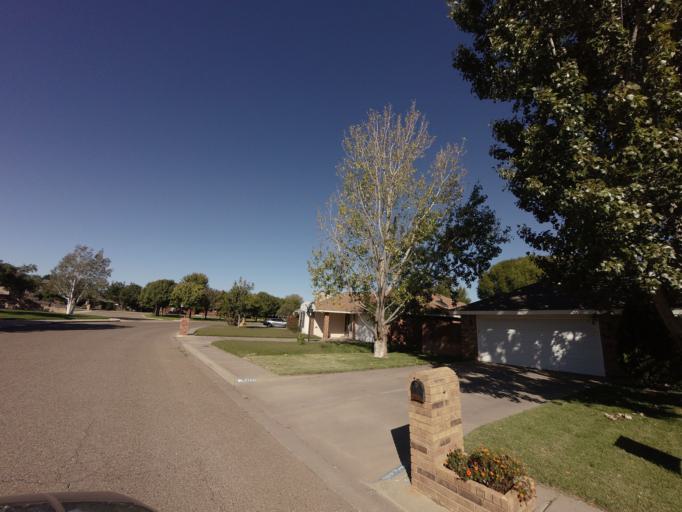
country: US
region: New Mexico
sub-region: Curry County
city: Clovis
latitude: 34.4289
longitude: -103.1753
